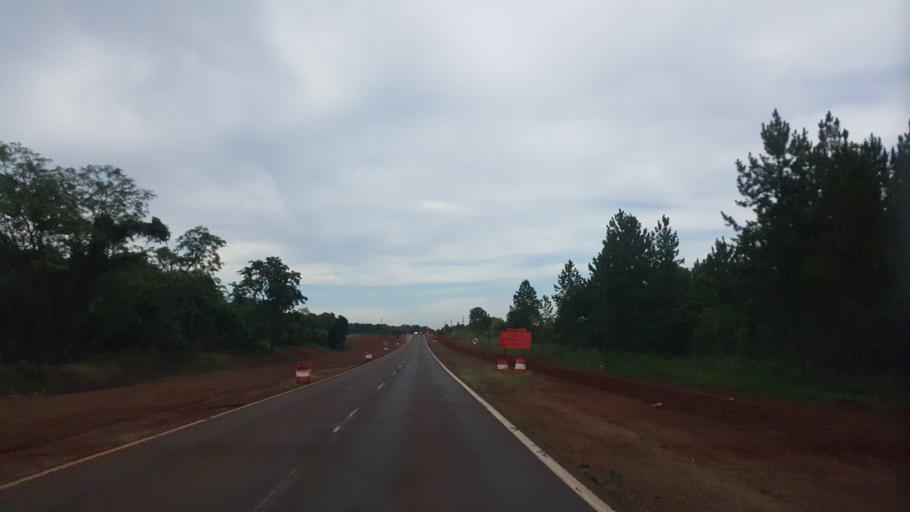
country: AR
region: Misiones
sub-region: Departamento de Candelaria
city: Loreto
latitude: -27.3420
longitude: -55.5458
